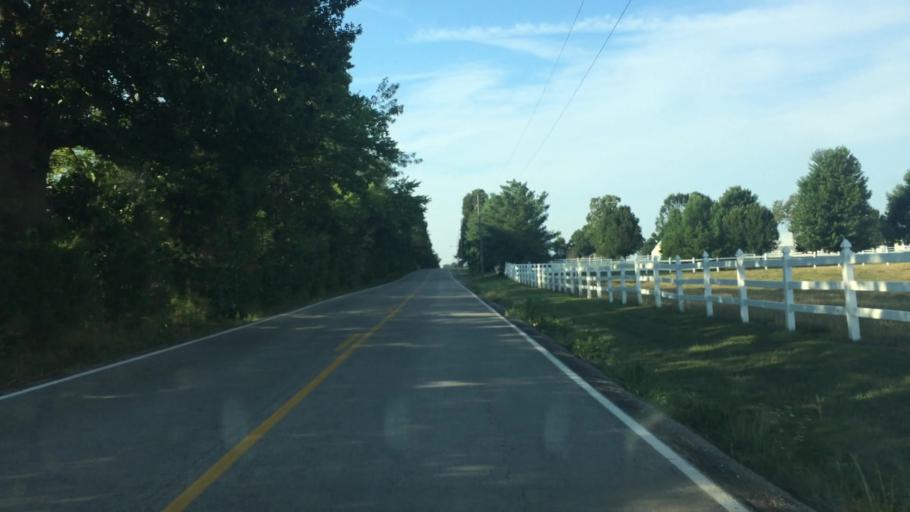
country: US
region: Missouri
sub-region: Greene County
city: Strafford
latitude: 37.2663
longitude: -93.1877
